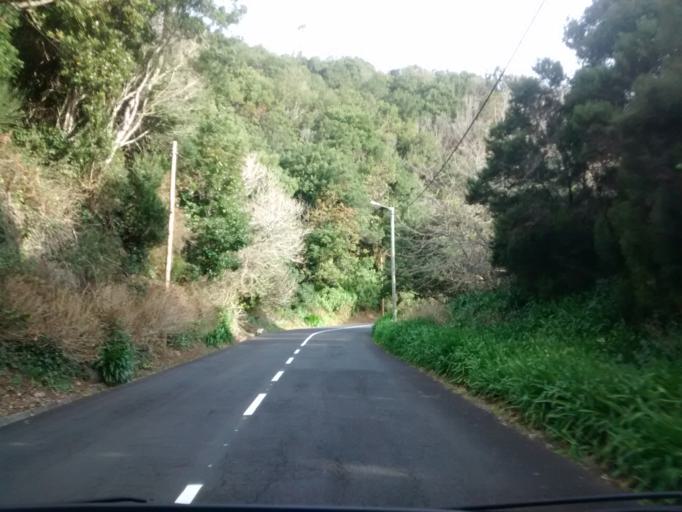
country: PT
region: Madeira
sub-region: Sao Vicente
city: Sao Vicente
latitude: 32.7503
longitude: -17.0254
